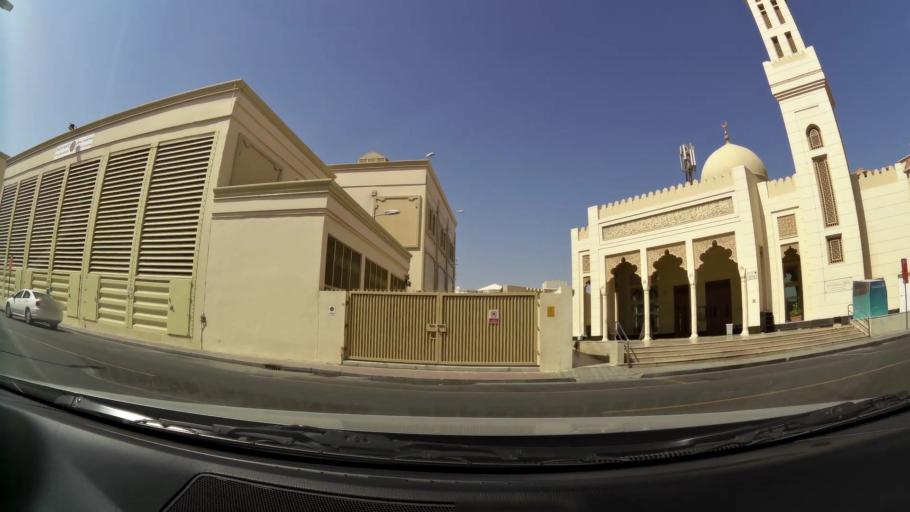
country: AE
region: Ash Shariqah
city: Sharjah
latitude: 25.2365
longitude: 55.2725
